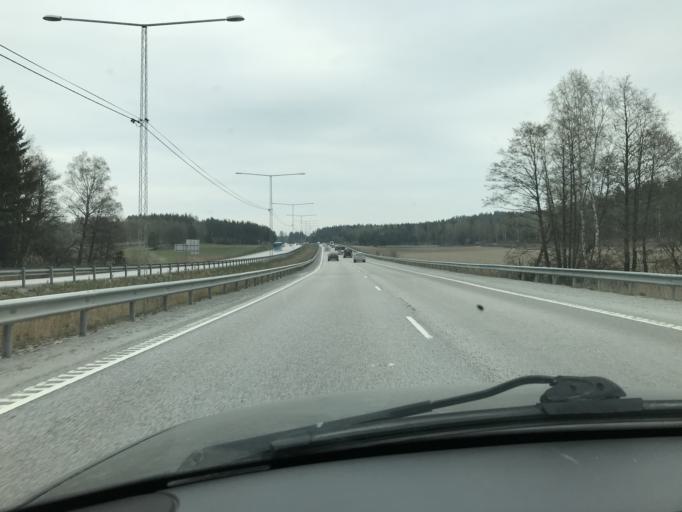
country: SE
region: Stockholm
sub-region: Taby Kommun
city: Taby
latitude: 59.4713
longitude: 18.1590
